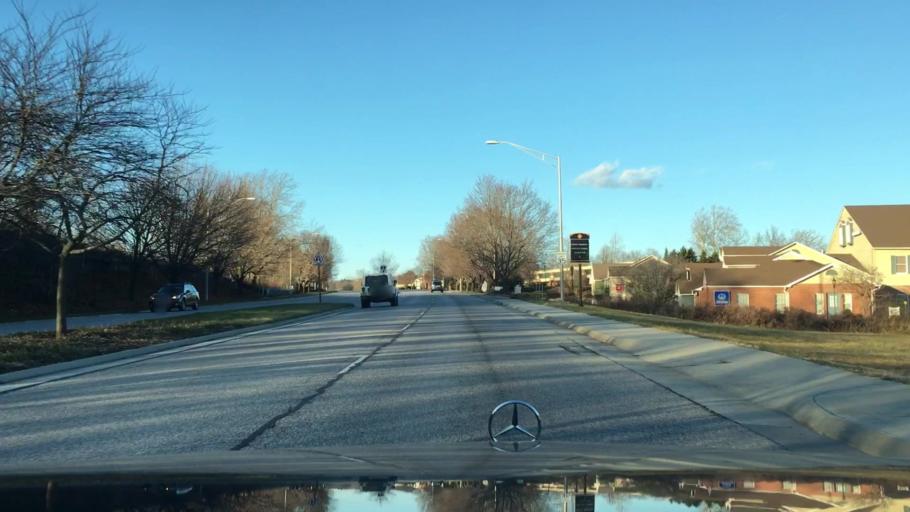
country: US
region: Virginia
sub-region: Montgomery County
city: Blacksburg
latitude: 37.2046
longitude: -80.3989
